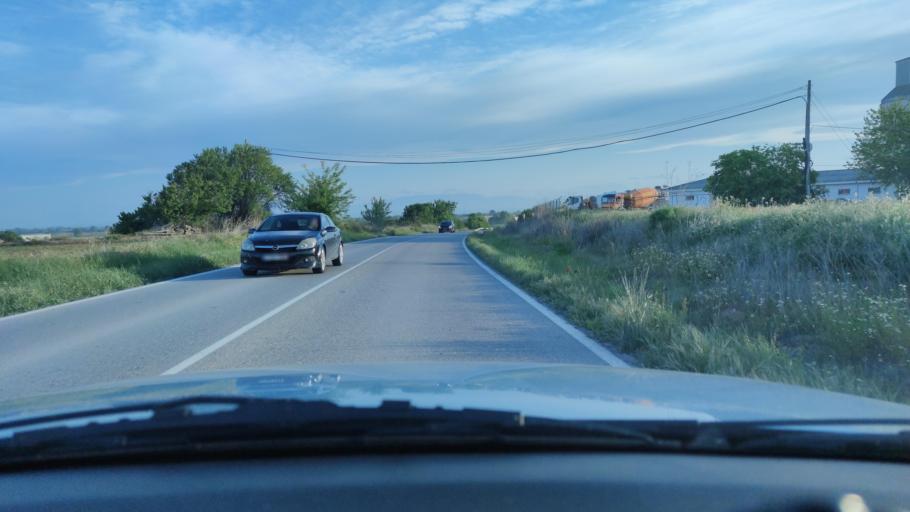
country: ES
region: Catalonia
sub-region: Provincia de Lleida
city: Bellpuig
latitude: 41.6398
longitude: 1.0012
